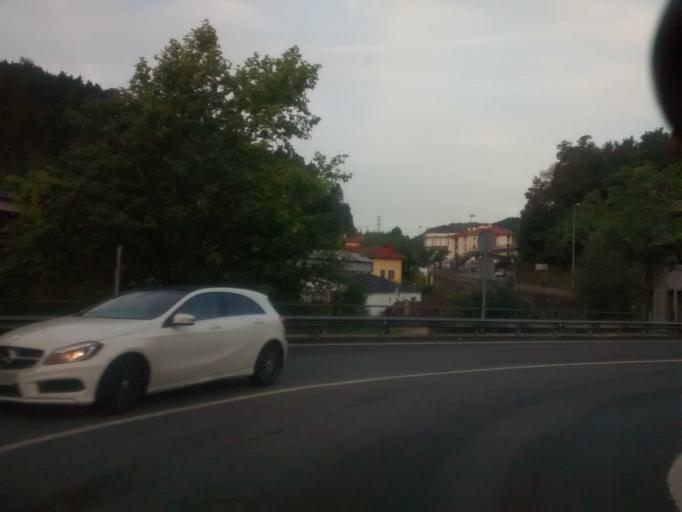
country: ES
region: Basque Country
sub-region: Provincia de Guipuzcoa
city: Eibar
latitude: 43.1903
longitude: -2.4499
